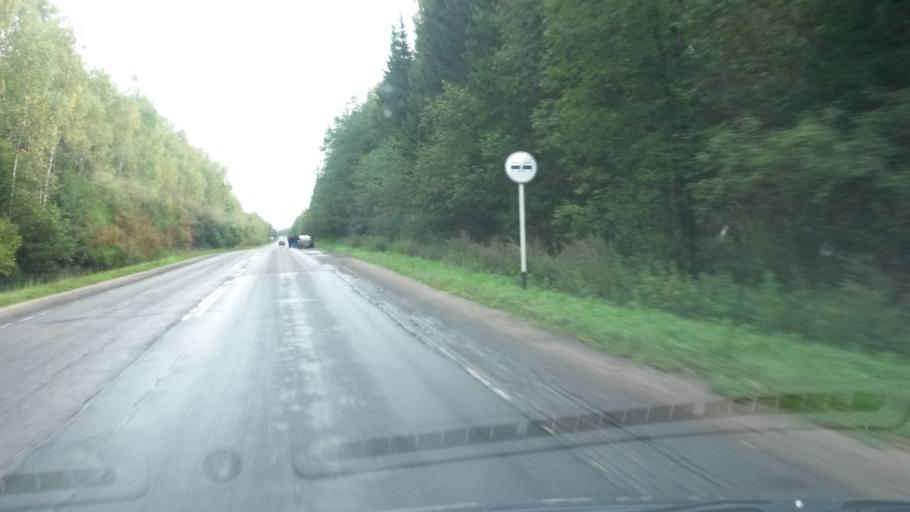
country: RU
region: Ivanovo
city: Kaminskiy
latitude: 57.0507
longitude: 41.3688
